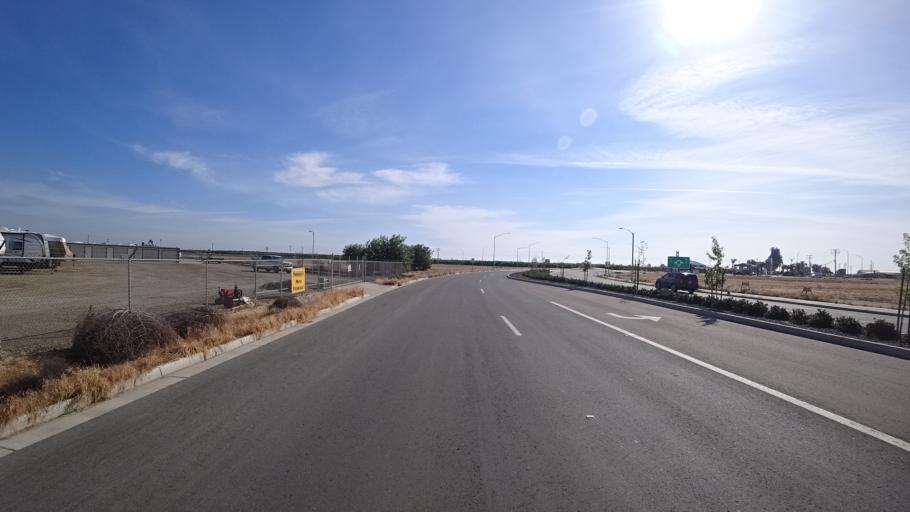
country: US
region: California
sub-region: Kings County
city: Home Garden
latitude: 36.3286
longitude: -119.6031
